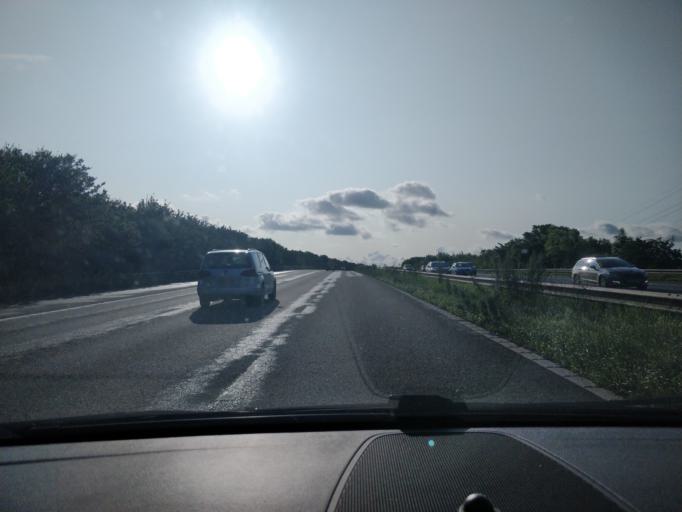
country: GB
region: England
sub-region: Sefton
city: Melling
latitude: 53.4848
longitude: -2.9241
